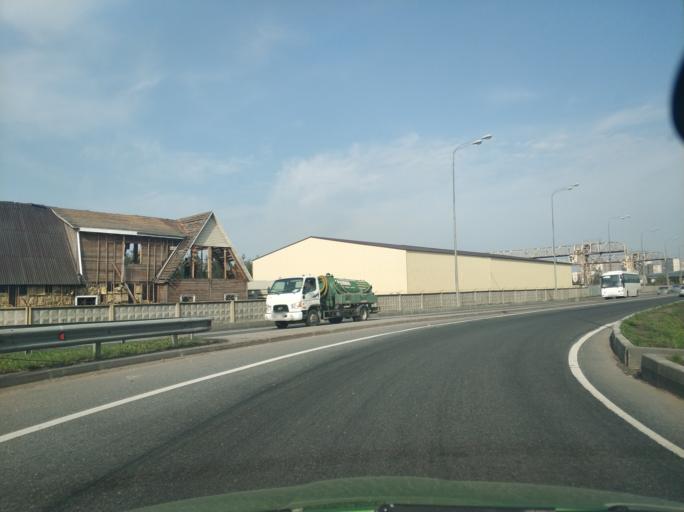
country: RU
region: Leningrad
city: Murino
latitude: 60.0350
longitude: 30.4394
